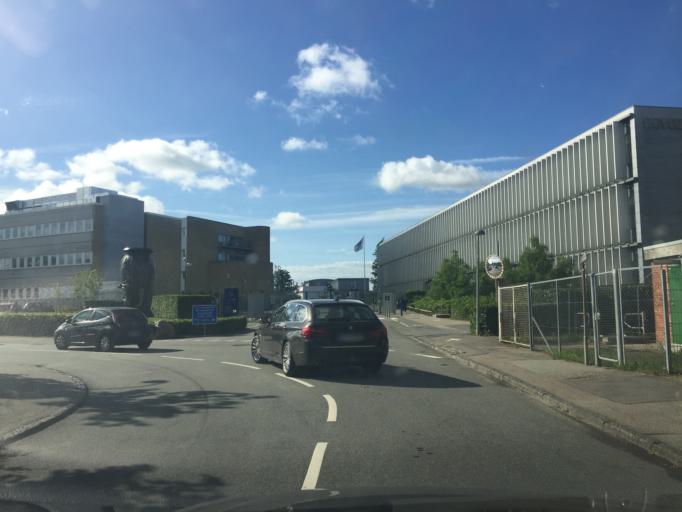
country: DK
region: Capital Region
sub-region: Herlev Kommune
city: Herlev
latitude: 55.7542
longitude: 12.4478
